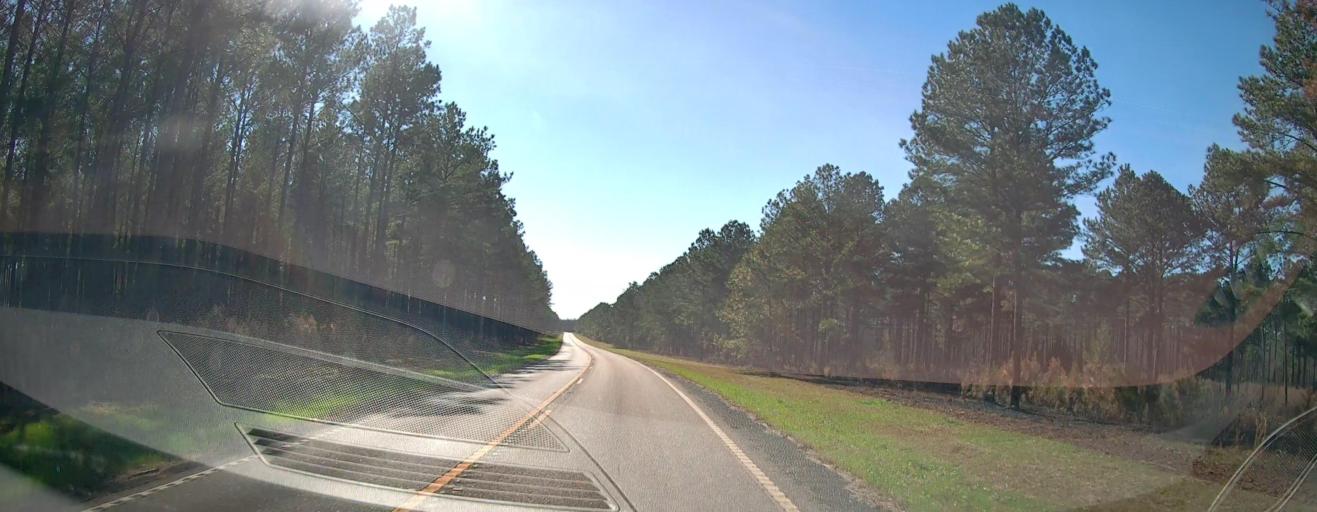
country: US
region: Georgia
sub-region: Schley County
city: Ellaville
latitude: 32.1901
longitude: -84.2329
